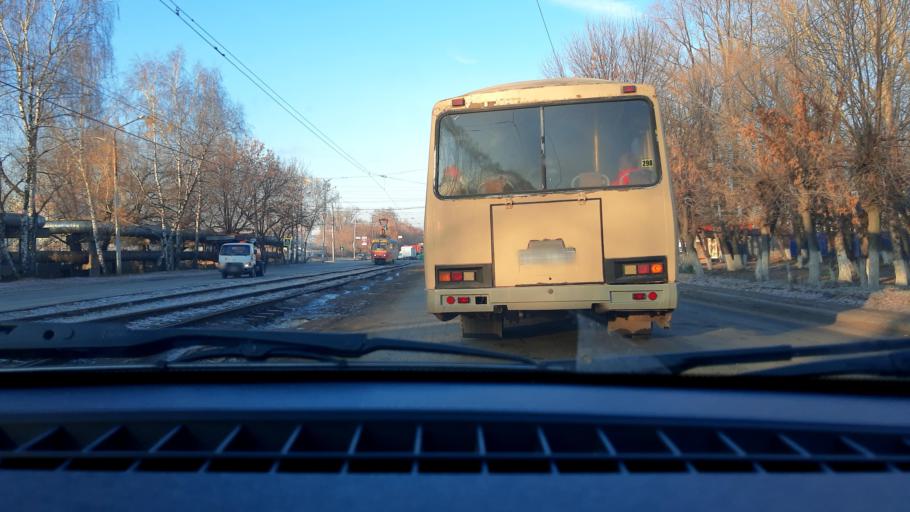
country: RU
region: Bashkortostan
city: Ufa
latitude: 54.7985
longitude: 56.0791
